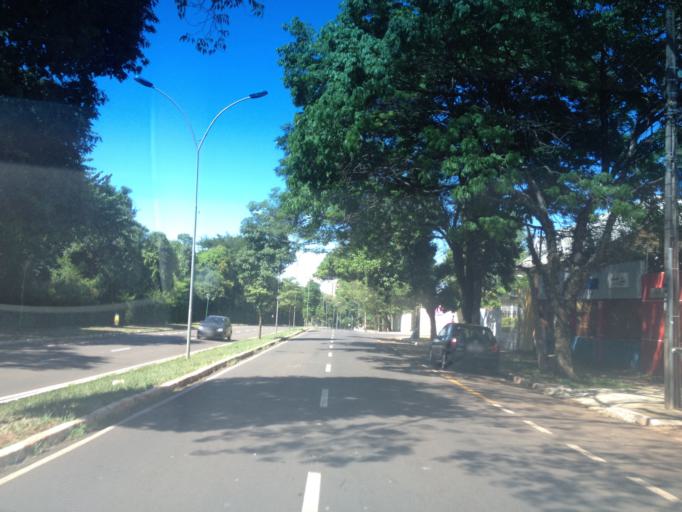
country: BR
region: Parana
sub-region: Maringa
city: Maringa
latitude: -23.4325
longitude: -51.9460
